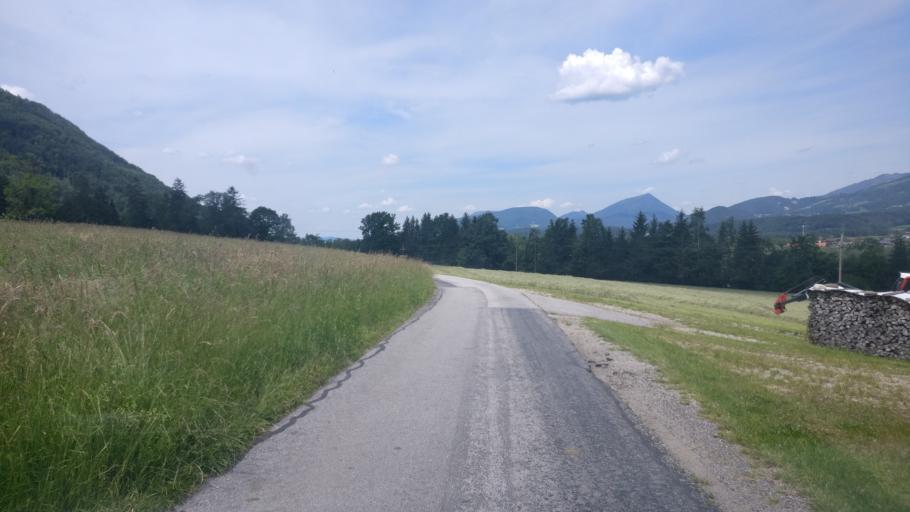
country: AT
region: Salzburg
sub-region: Politischer Bezirk Hallein
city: Kuchl
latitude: 47.6353
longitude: 13.1287
